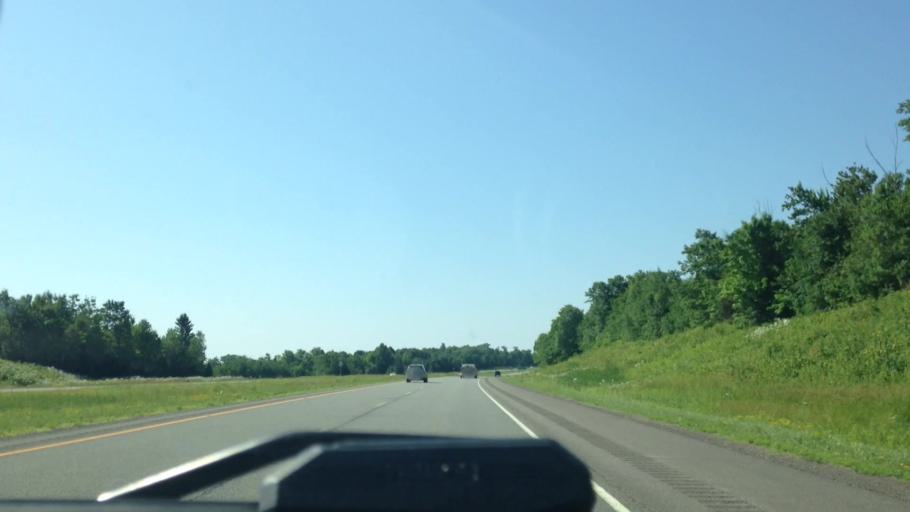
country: US
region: Wisconsin
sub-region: Douglas County
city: Lake Nebagamon
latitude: 46.4230
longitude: -91.8103
